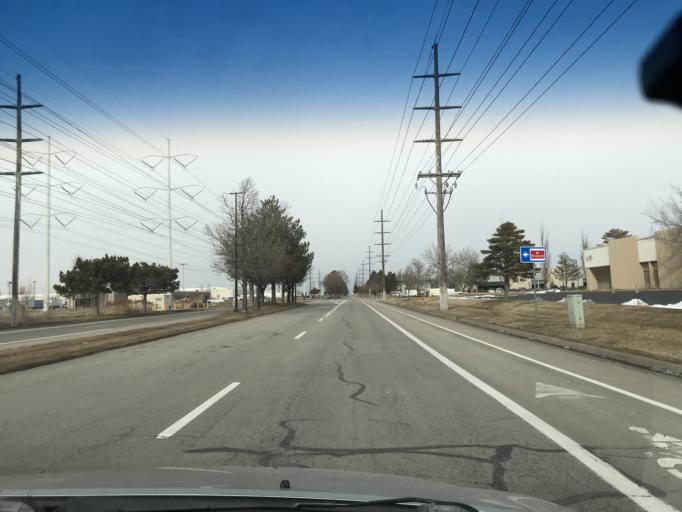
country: US
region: Utah
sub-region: Salt Lake County
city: West Valley City
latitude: 40.7750
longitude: -112.0056
